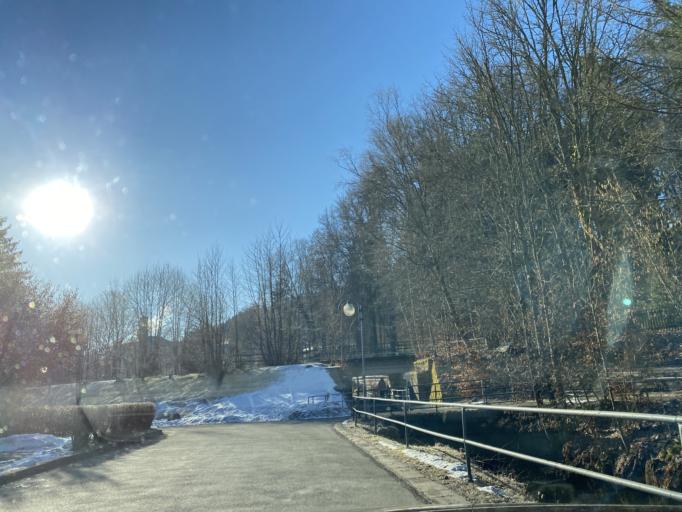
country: DE
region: Saxony
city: Thermalbad Wiesenbad
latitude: 50.6205
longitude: 13.0414
